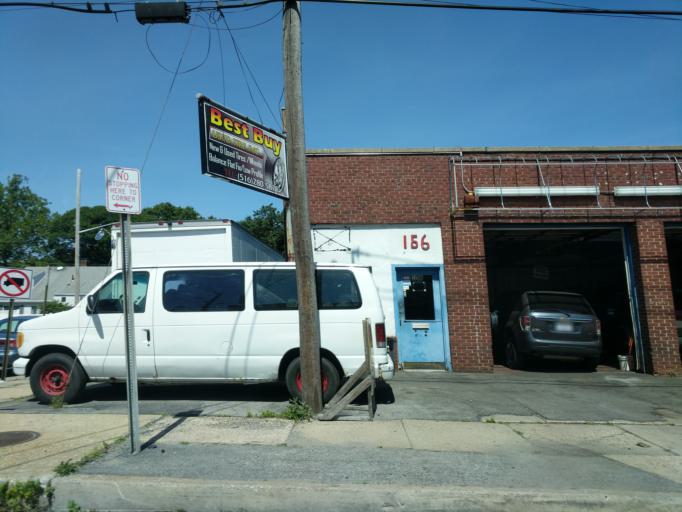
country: US
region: New York
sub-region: Nassau County
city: Rockville Centre
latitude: 40.6495
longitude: -73.6371
